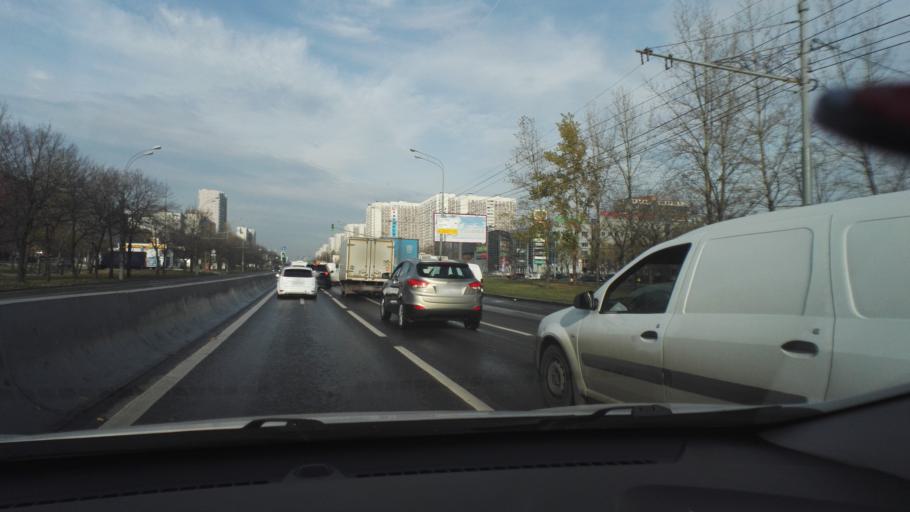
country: RU
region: Moscow
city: Altuf'yevskiy
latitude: 55.8846
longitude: 37.5858
